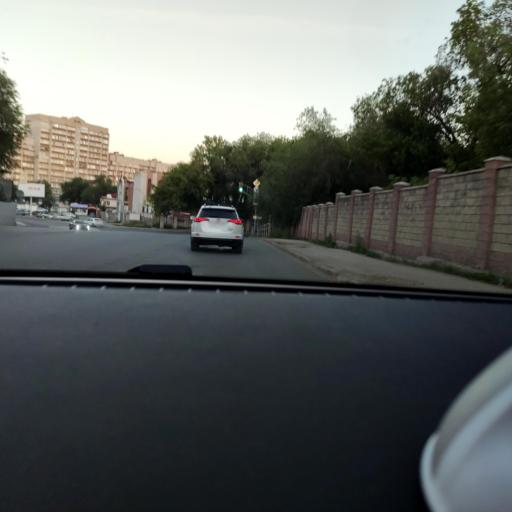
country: RU
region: Samara
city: Petra-Dubrava
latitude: 53.2413
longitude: 50.2730
